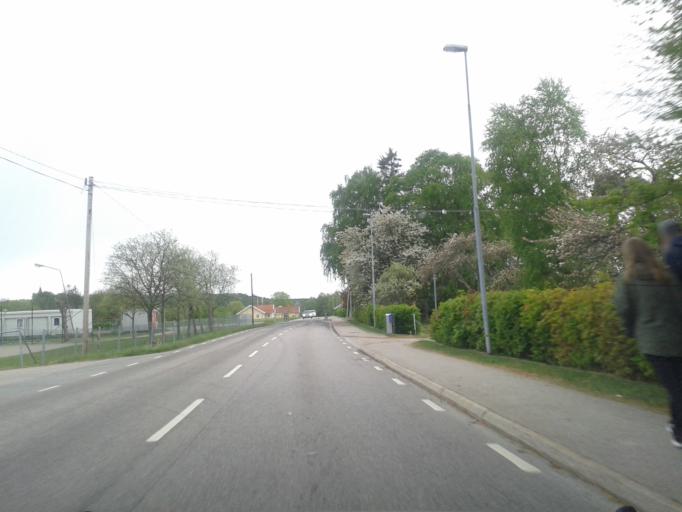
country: SE
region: Vaestra Goetaland
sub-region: Stenungsunds Kommun
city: Stora Hoga
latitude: 57.9851
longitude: 11.8283
